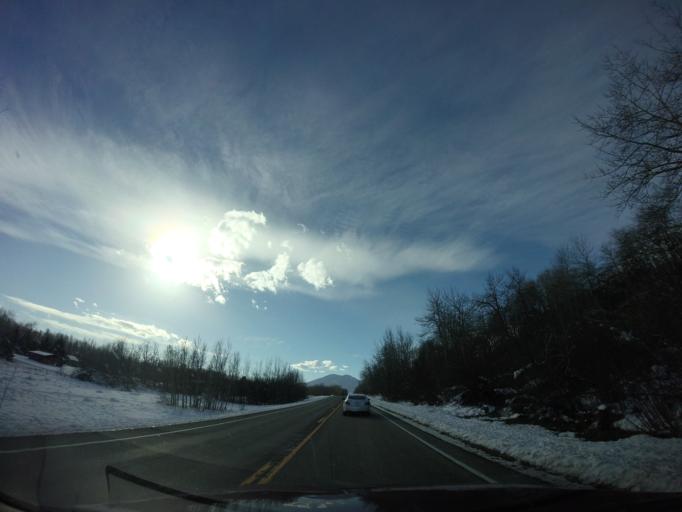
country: US
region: Montana
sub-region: Carbon County
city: Red Lodge
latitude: 45.2282
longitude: -109.2391
